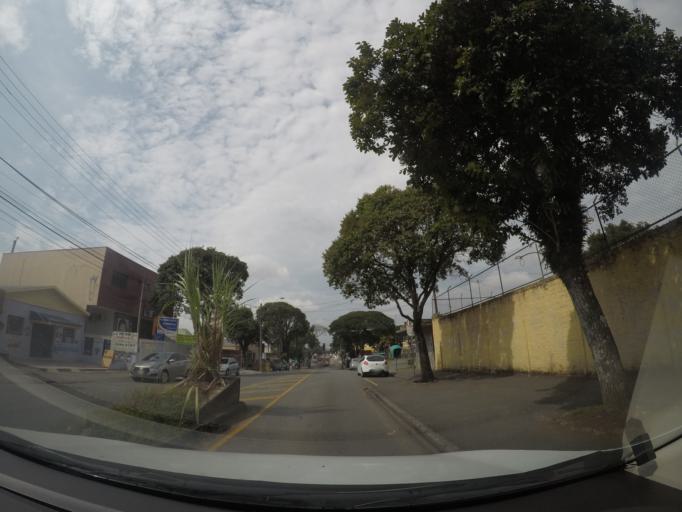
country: BR
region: Parana
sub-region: Sao Jose Dos Pinhais
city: Sao Jose dos Pinhais
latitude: -25.5153
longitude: -49.2762
